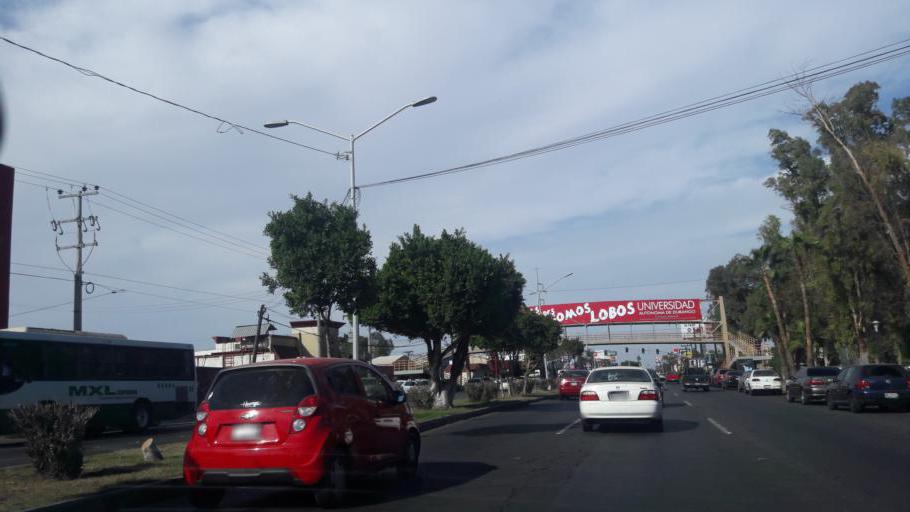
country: MX
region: Baja California
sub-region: Mexicali
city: Mexicali
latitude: 32.6329
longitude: -115.4468
